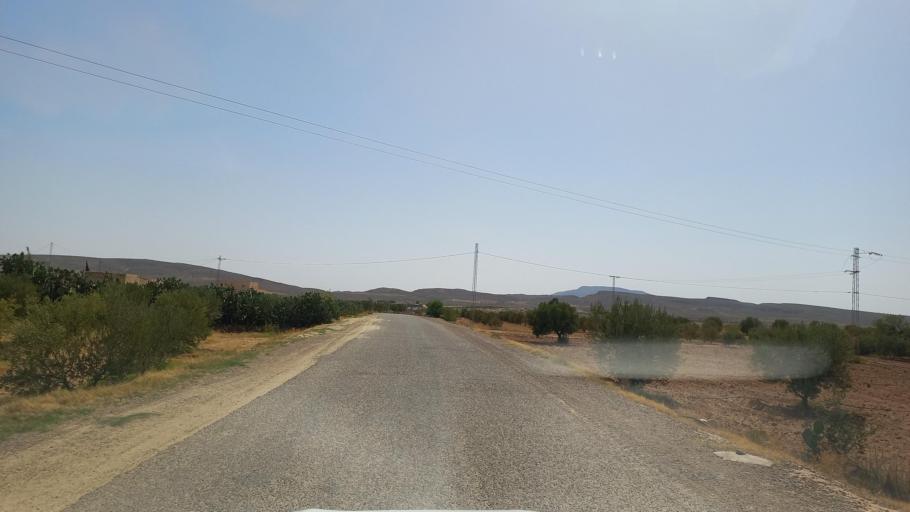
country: TN
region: Al Qasrayn
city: Kasserine
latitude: 35.2109
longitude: 9.0417
